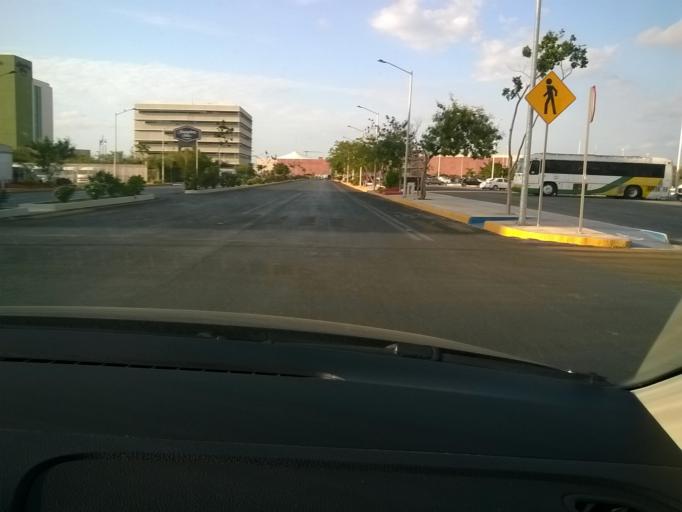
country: MX
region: Yucatan
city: Merida
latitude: 21.0338
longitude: -89.6317
